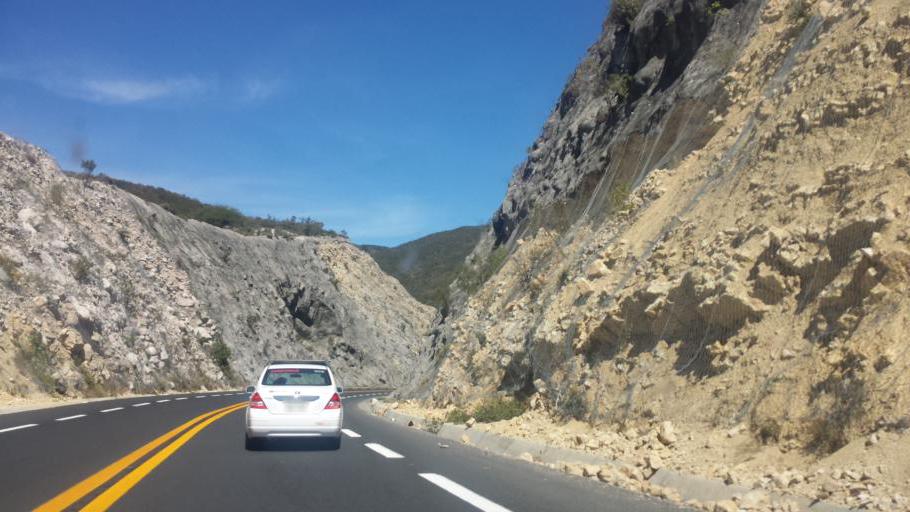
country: MX
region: Puebla
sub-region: San Jose Miahuatlan
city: San Pedro Tetitlan
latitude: 18.0184
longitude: -97.3524
